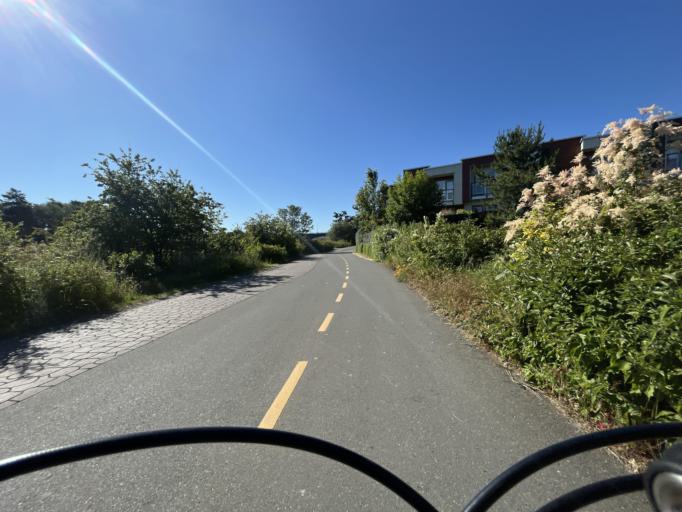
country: CA
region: British Columbia
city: Victoria
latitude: 48.4361
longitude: -123.3802
